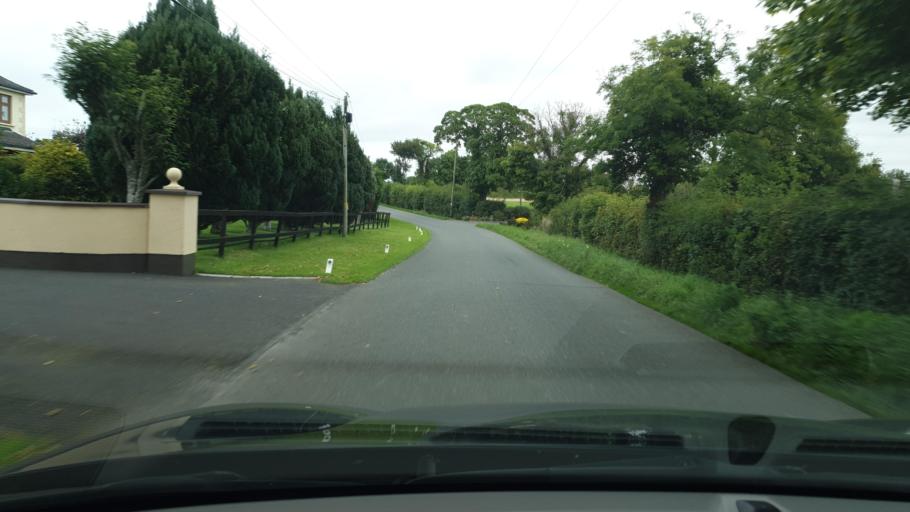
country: IE
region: Leinster
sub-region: An Mhi
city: Ratoath
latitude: 53.4816
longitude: -6.5027
